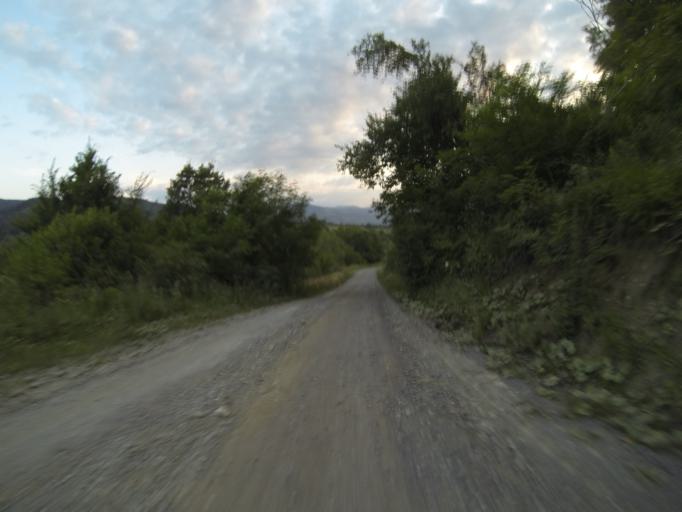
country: RO
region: Brasov
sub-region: Comuna Sinca Noua
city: Sinca Noua
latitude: 45.7145
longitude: 25.2659
